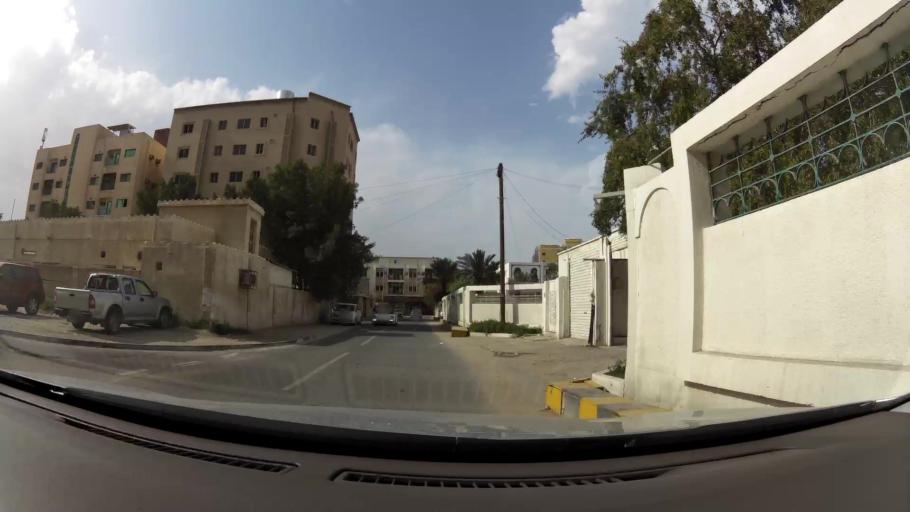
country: QA
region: Baladiyat ad Dawhah
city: Doha
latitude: 25.2786
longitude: 51.5094
